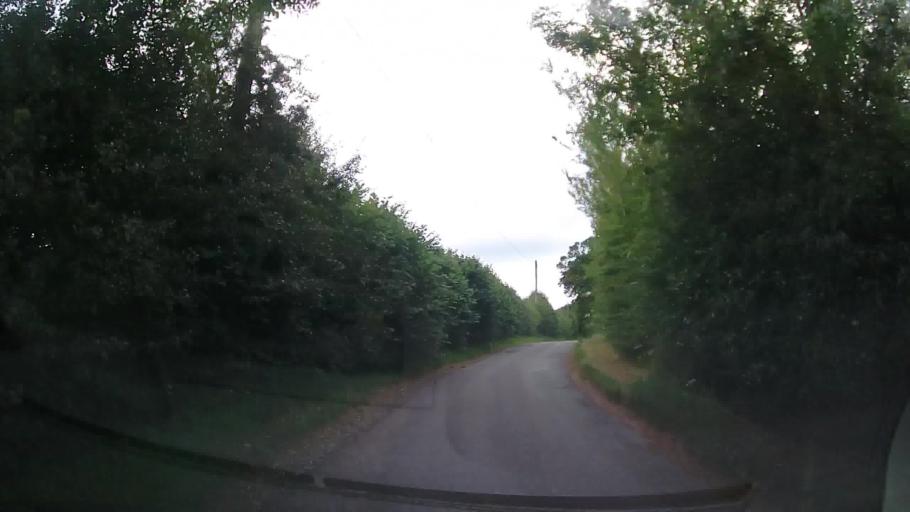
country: GB
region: England
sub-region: Shropshire
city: Whitchurch
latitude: 52.9345
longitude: -2.7240
